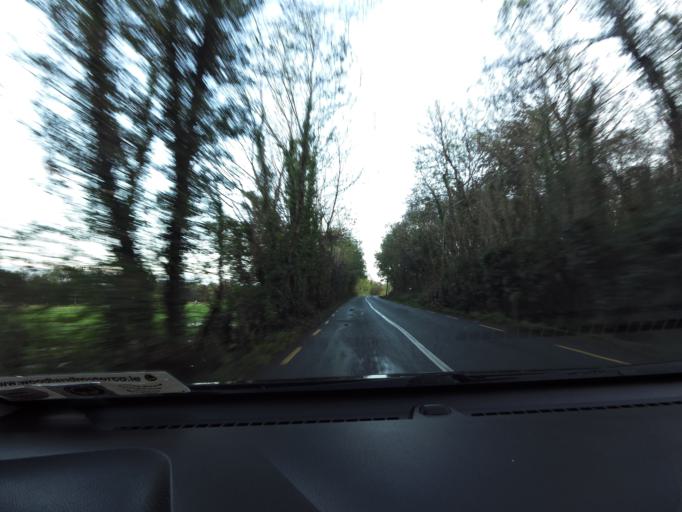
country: IE
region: Connaught
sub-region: County Galway
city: Tuam
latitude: 53.5040
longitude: -8.6092
